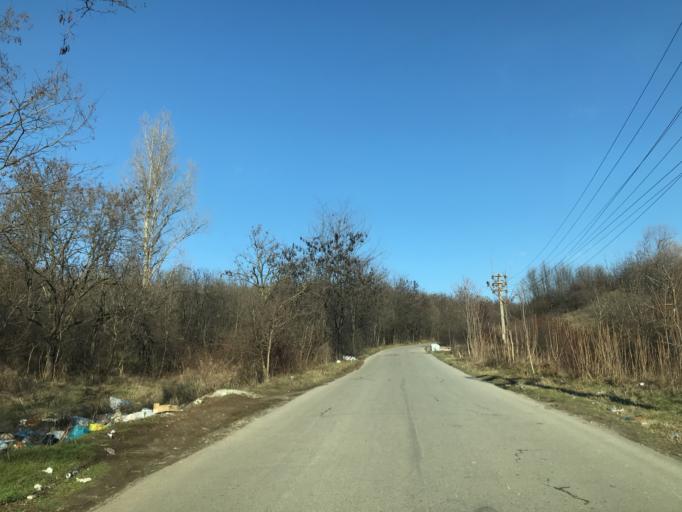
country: RO
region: Olt
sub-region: Municipiul Slatina
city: Slatina
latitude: 44.4104
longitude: 24.3593
